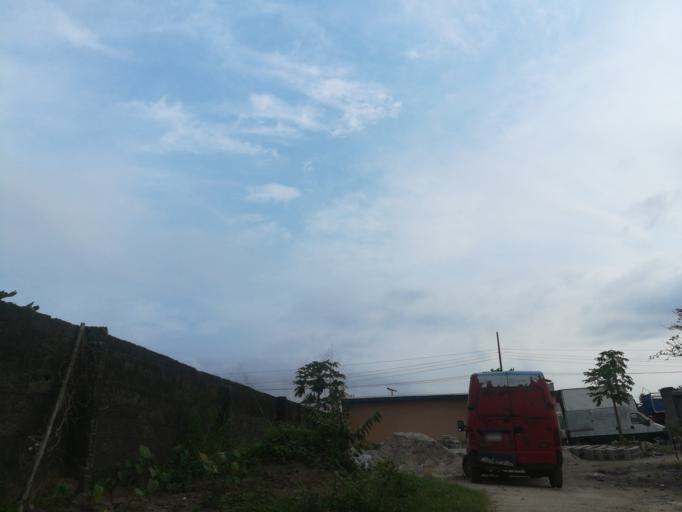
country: NG
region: Rivers
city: Okrika
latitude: 4.7625
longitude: 7.0872
